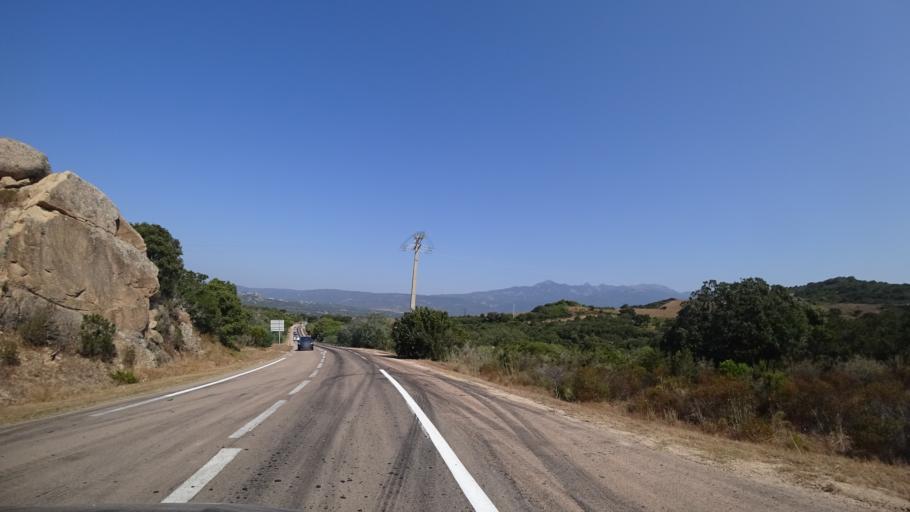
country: FR
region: Corsica
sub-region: Departement de la Corse-du-Sud
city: Bonifacio
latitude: 41.4707
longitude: 9.0954
